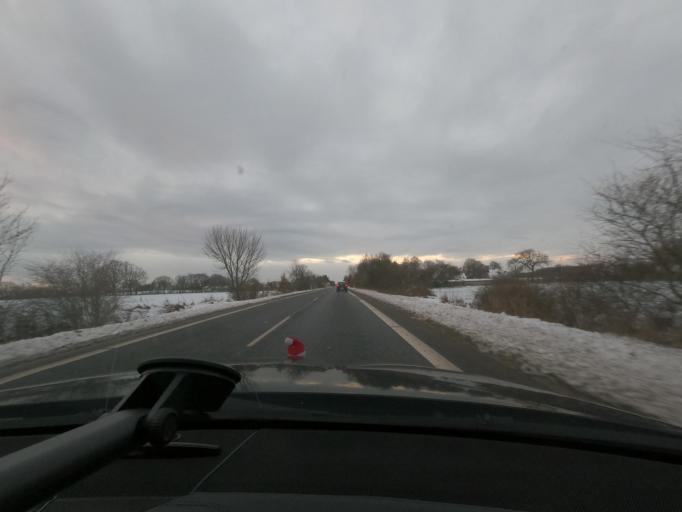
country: DE
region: Schleswig-Holstein
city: Wees
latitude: 54.8826
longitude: 9.4792
